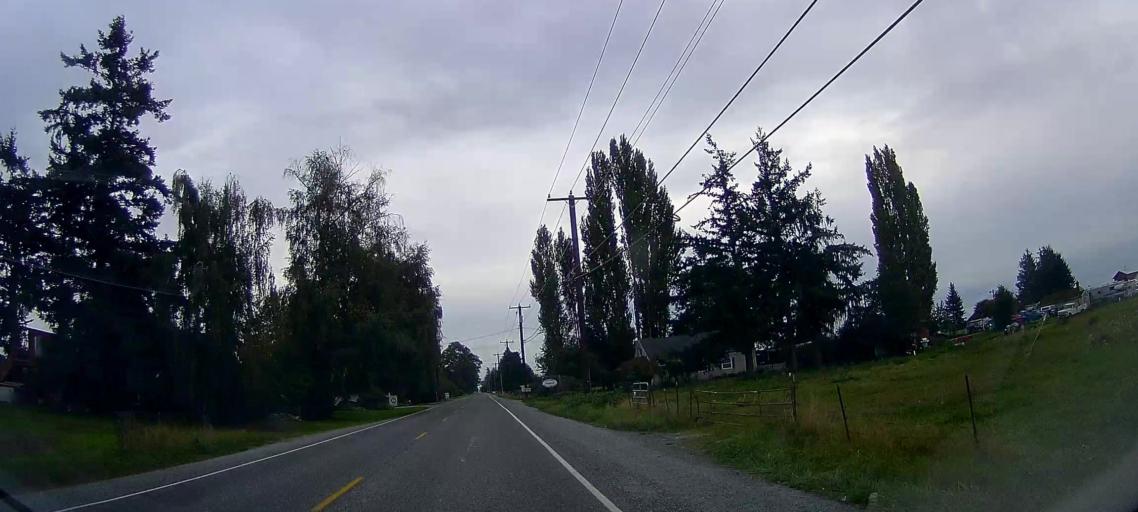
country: US
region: Washington
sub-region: Skagit County
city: Mount Vernon
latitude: 48.4530
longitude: -122.3786
